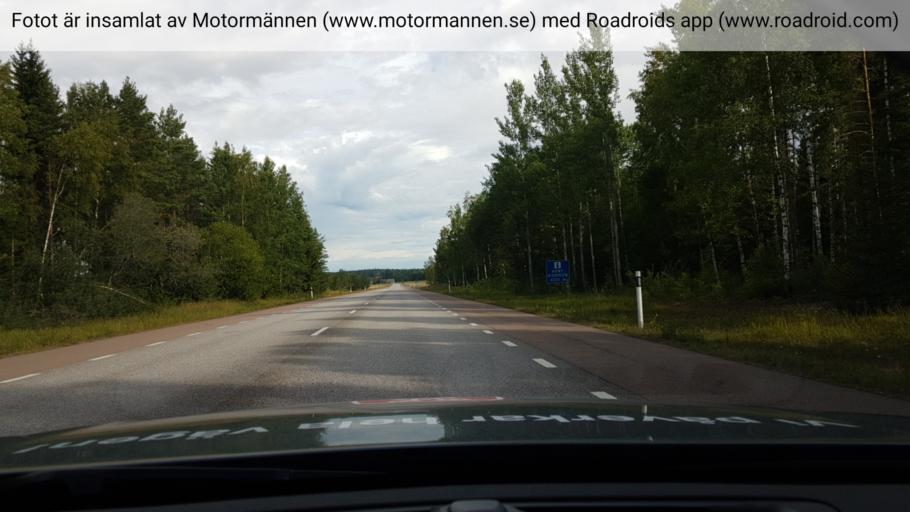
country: SE
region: Uppsala
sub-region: Heby Kommun
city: Morgongava
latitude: 59.8698
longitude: 16.9247
